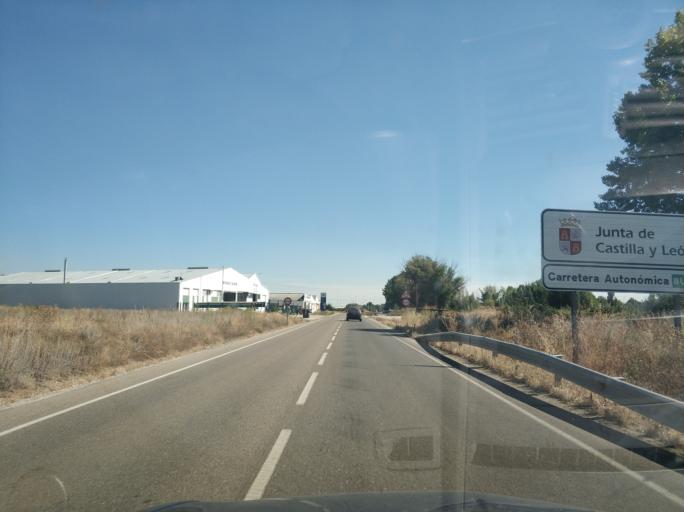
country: ES
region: Castille and Leon
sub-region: Provincia de Burgos
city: Aranda de Duero
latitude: 41.6754
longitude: -3.6640
